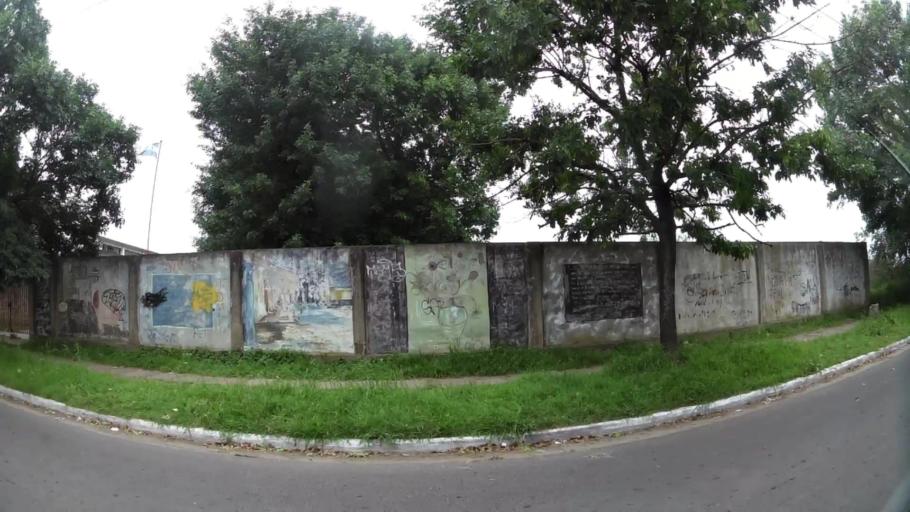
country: AR
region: Buenos Aires
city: San Justo
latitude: -34.7145
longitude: -58.5390
